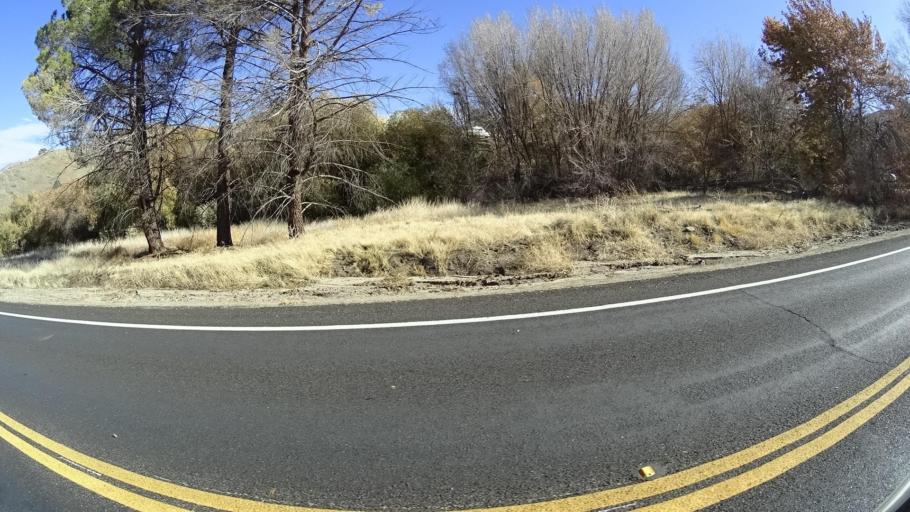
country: US
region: California
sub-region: Kern County
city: Bodfish
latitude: 35.5938
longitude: -118.4924
